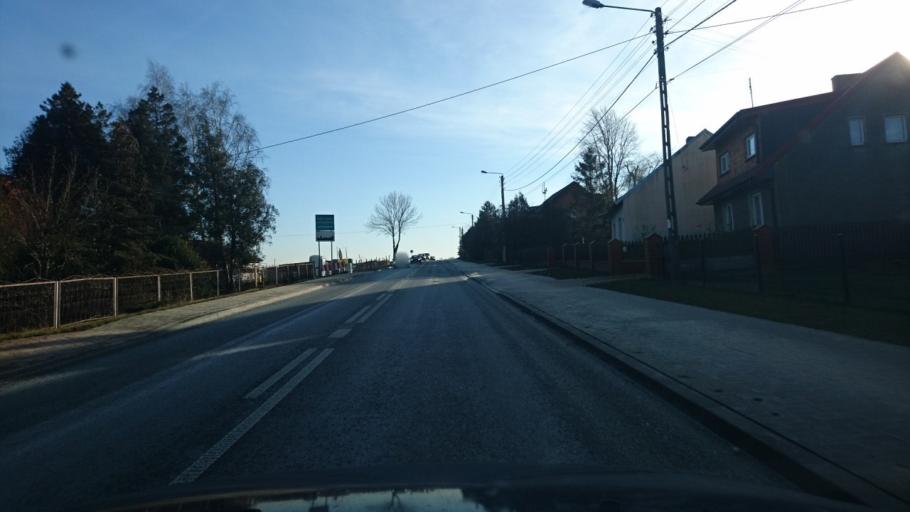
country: PL
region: Silesian Voivodeship
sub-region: Powiat klobucki
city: Starokrzepice
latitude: 51.0211
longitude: 18.6509
